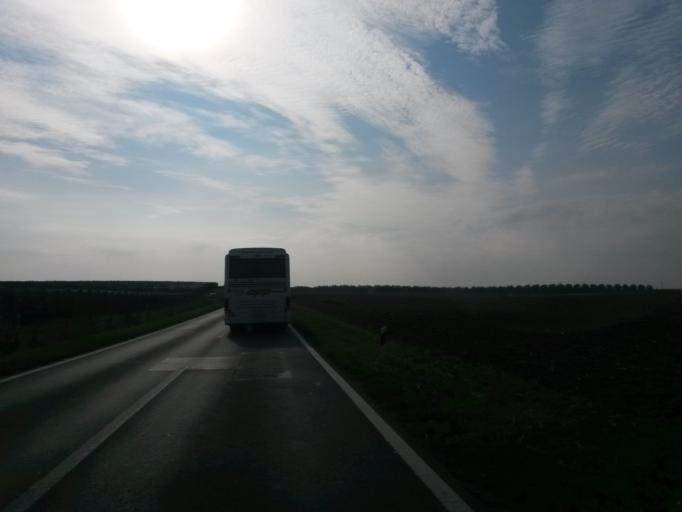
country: HR
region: Vukovarsko-Srijemska
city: Vukovar
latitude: 45.3106
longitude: 19.0775
